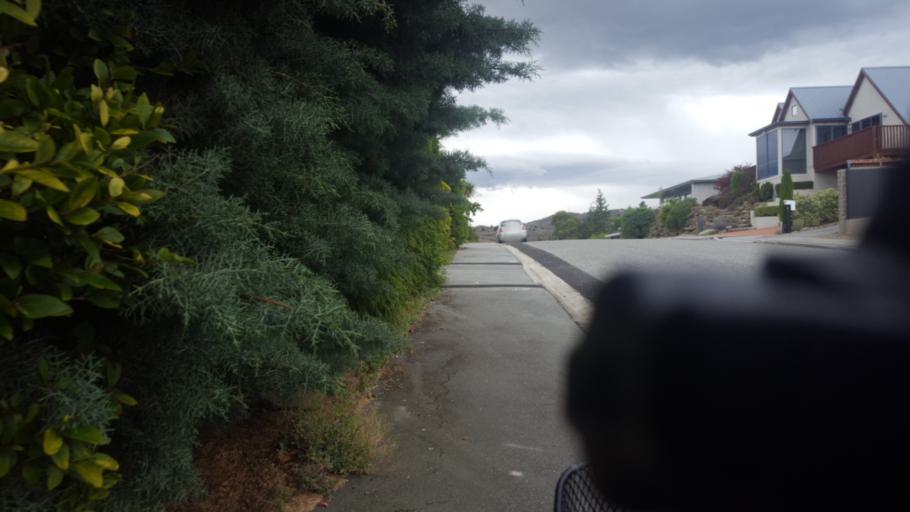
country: NZ
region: Otago
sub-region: Queenstown-Lakes District
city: Wanaka
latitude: -45.2625
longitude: 169.3786
